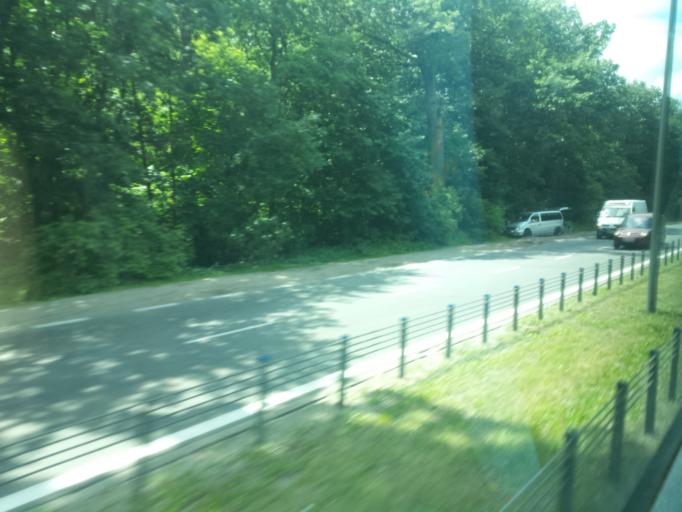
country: PL
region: Masovian Voivodeship
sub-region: Warszawa
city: Wawer
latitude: 52.2257
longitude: 21.1676
